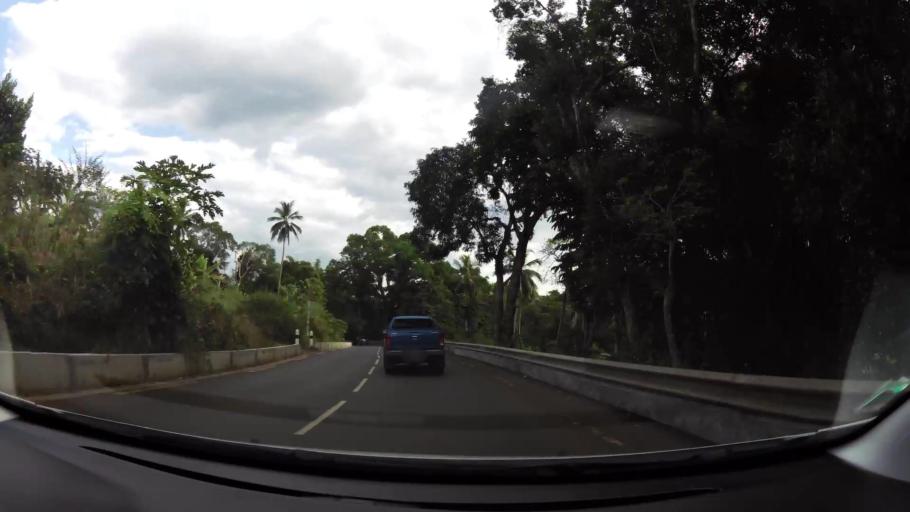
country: YT
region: Ouangani
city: Ouangani
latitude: -12.8358
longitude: 45.1548
